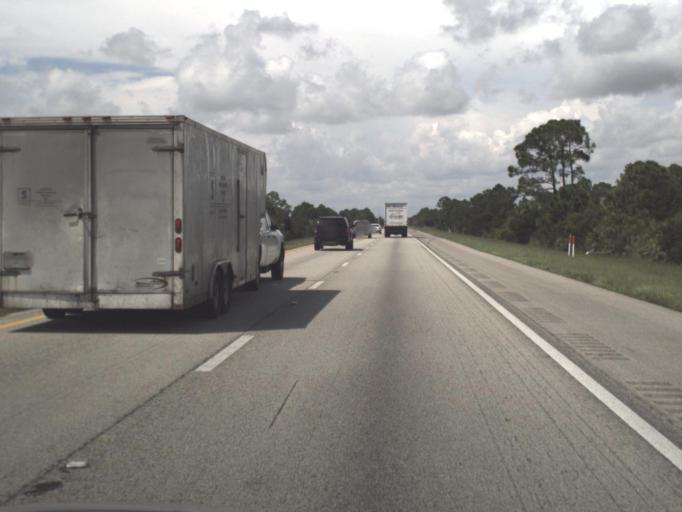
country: US
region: Florida
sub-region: Lee County
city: Burnt Store Marina
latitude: 26.8290
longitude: -81.9523
